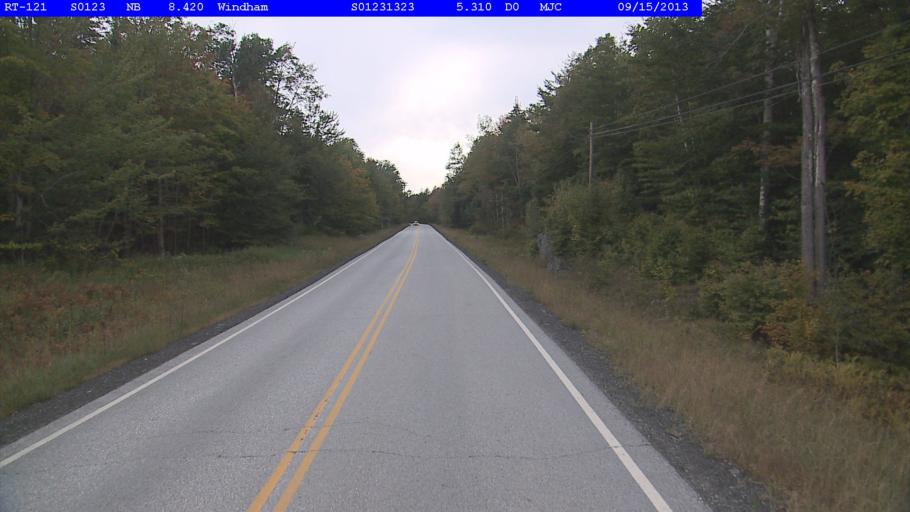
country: US
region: Vermont
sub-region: Windsor County
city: Chester
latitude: 43.1982
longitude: -72.7219
